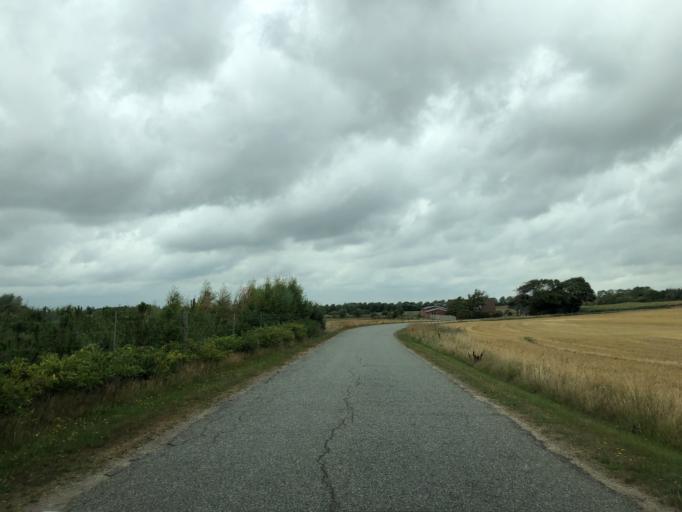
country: DK
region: Central Jutland
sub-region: Ringkobing-Skjern Kommune
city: Videbaek
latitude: 56.1040
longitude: 8.4890
